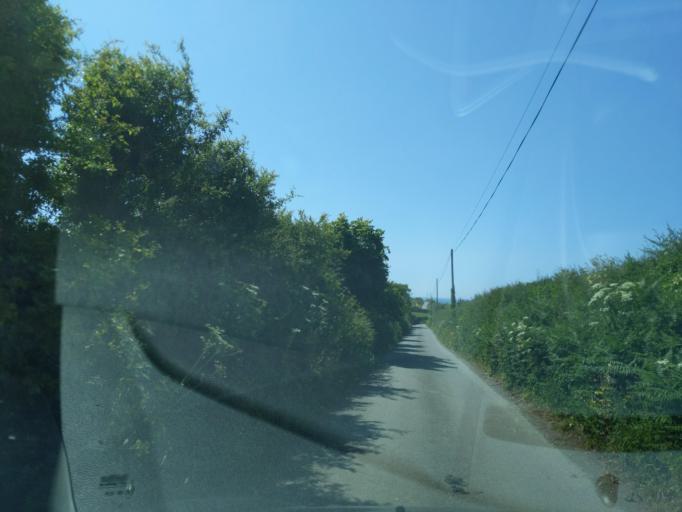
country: GB
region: England
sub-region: Cornwall
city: Wadebridge
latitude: 50.5841
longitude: -4.8479
